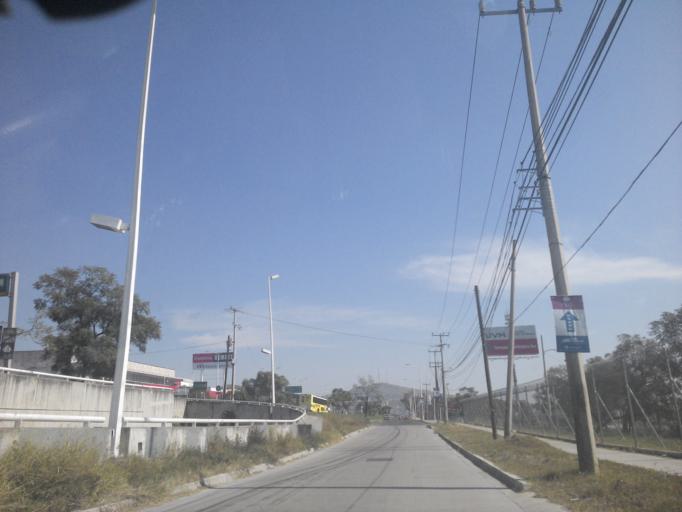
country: MX
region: Jalisco
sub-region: Tlajomulco de Zuniga
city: La Tijera
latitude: 20.6090
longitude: -103.4110
